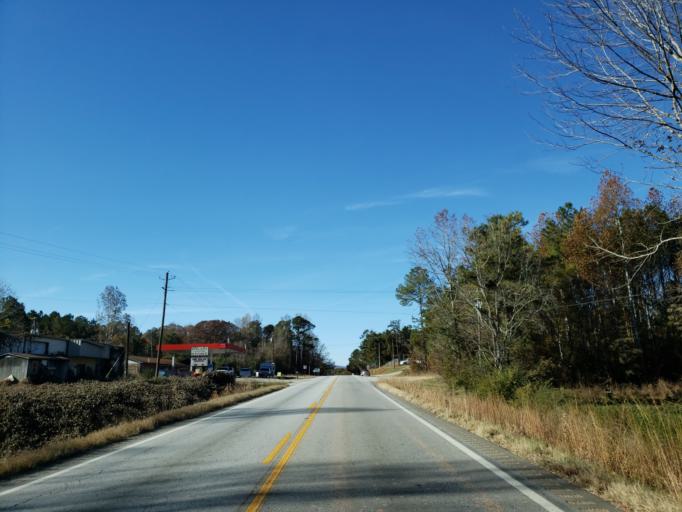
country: US
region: Alabama
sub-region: Calhoun County
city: Choccolocco
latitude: 33.5852
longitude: -85.6802
